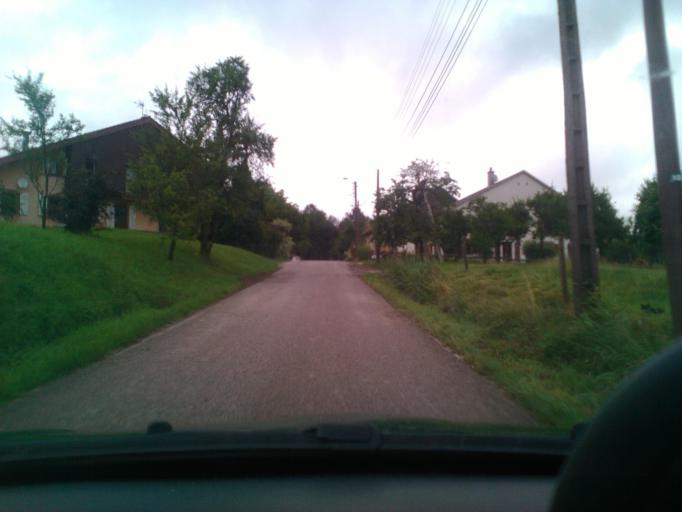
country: FR
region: Lorraine
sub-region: Departement des Vosges
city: Saint-Michel-sur-Meurthe
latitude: 48.3237
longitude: 6.9186
